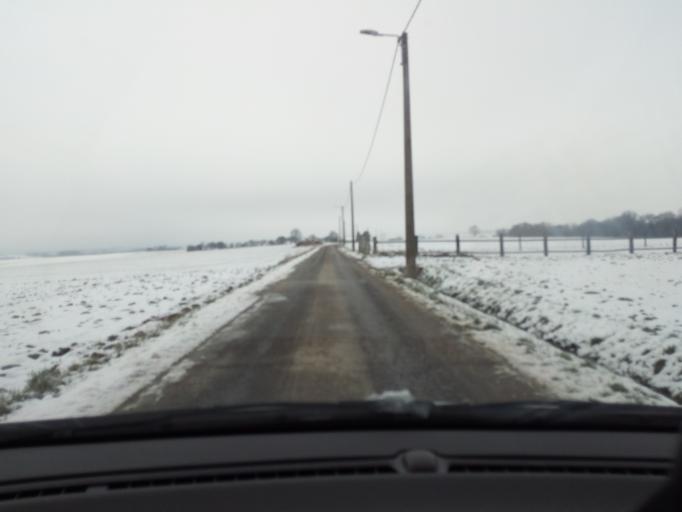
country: FR
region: Nord-Pas-de-Calais
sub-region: Departement du Nord
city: Boussois
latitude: 50.3606
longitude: 4.0261
